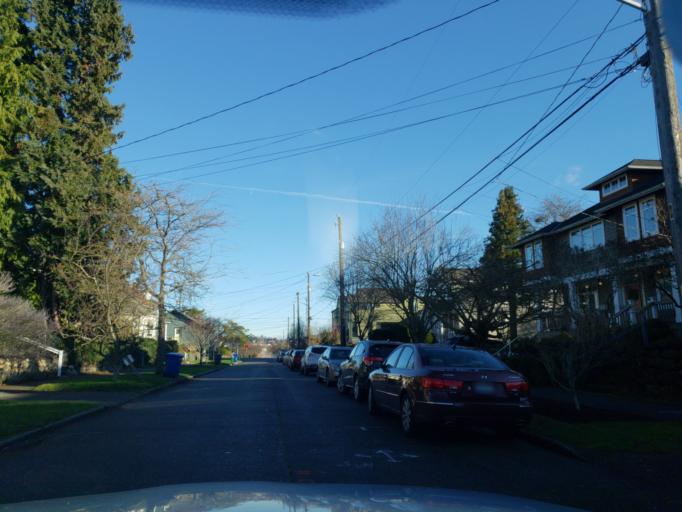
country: US
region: Washington
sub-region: King County
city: Shoreline
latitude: 47.6803
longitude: -122.3488
